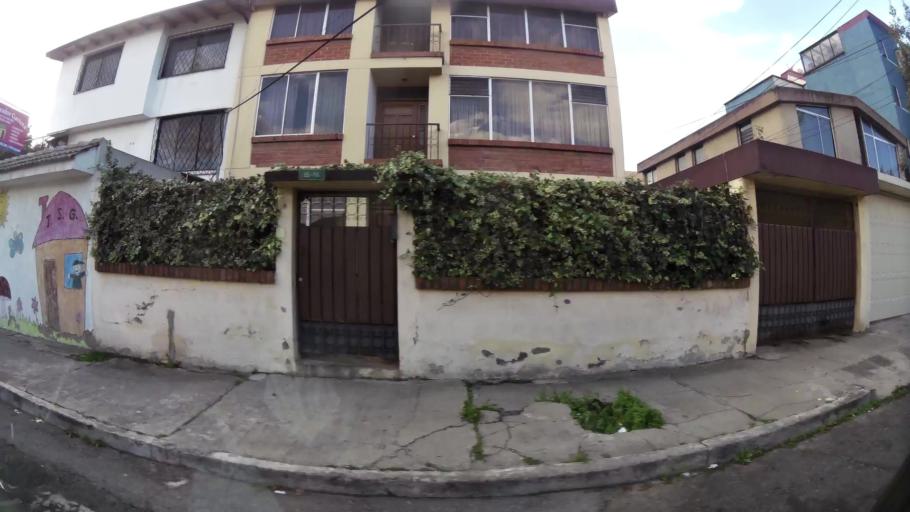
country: EC
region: Pichincha
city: Quito
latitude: -0.1342
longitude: -78.4795
